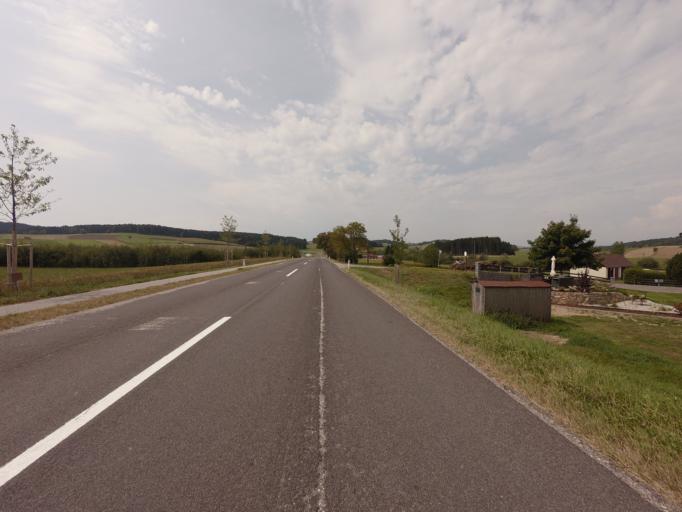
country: AT
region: Upper Austria
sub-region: Politischer Bezirk Urfahr-Umgebung
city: Reichenthal
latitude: 48.5518
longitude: 14.4389
